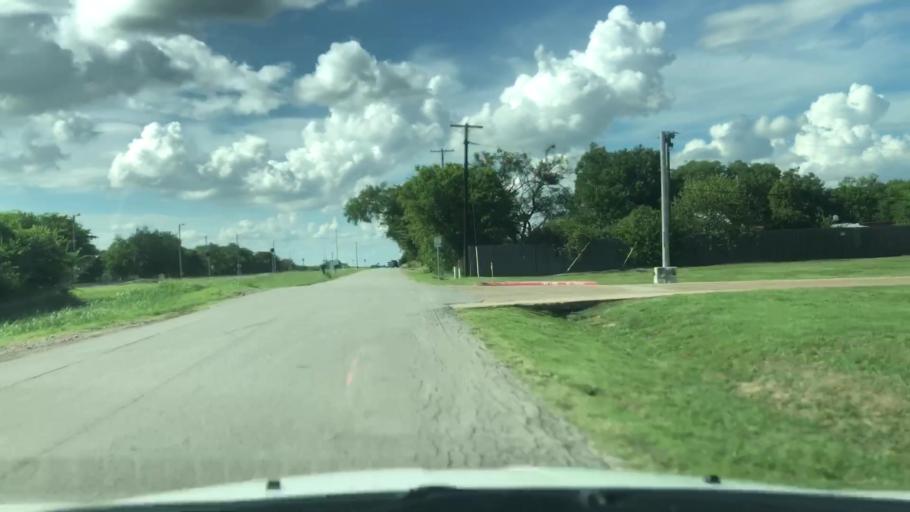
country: US
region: Texas
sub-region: Ellis County
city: Ennis
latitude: 32.3493
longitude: -96.6410
